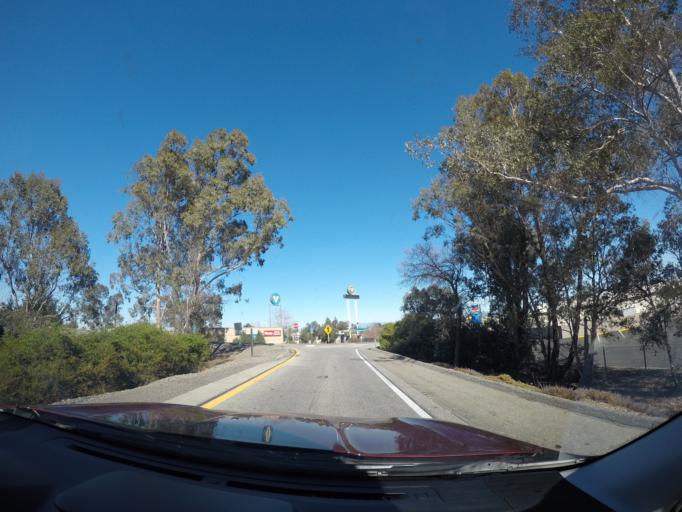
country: US
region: California
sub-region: Tehama County
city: Corning
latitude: 39.9277
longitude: -122.1989
